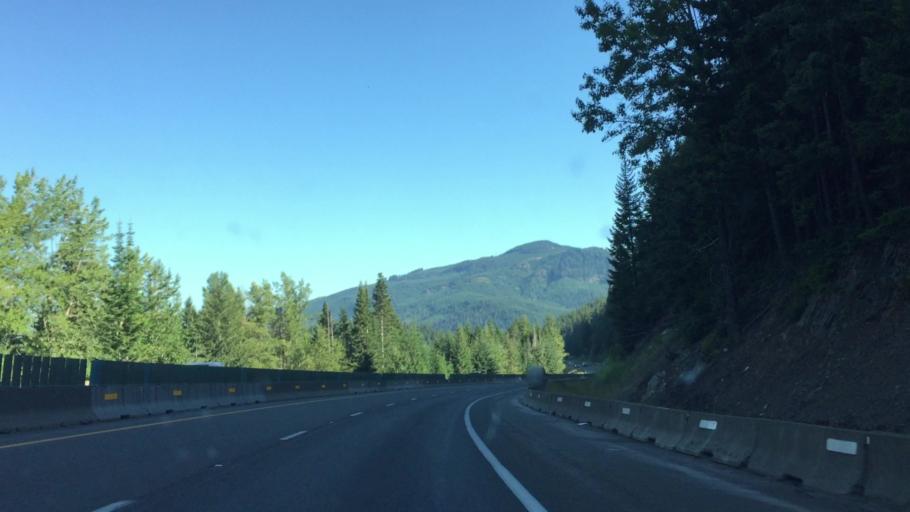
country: US
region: Washington
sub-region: Kittitas County
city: Cle Elum
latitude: 47.2808
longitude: -121.2777
